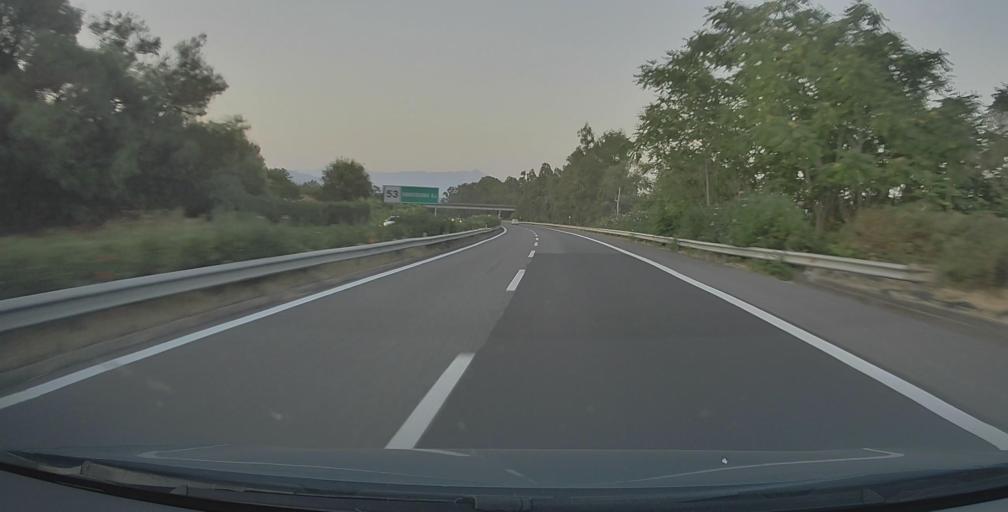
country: IT
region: Sicily
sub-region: Catania
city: Nunziata
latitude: 37.7598
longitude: 15.1803
